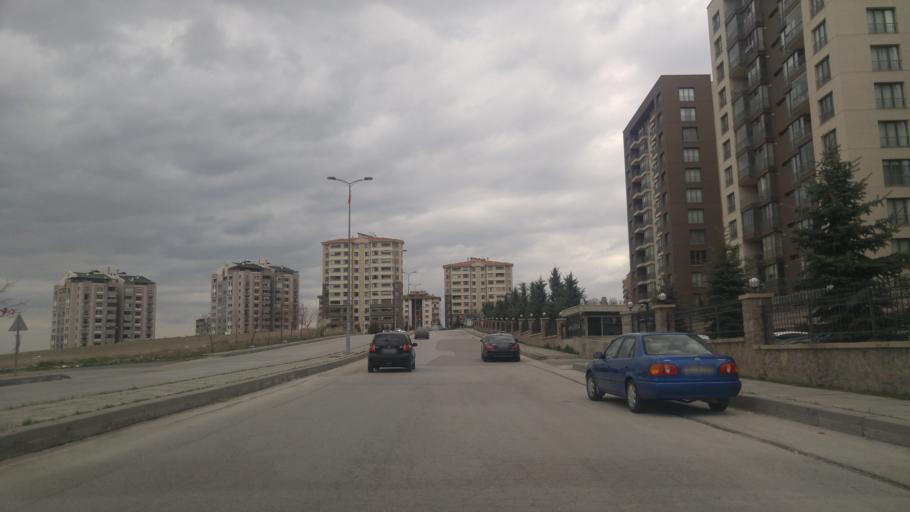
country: TR
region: Ankara
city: Etimesgut
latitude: 39.8662
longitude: 32.6414
